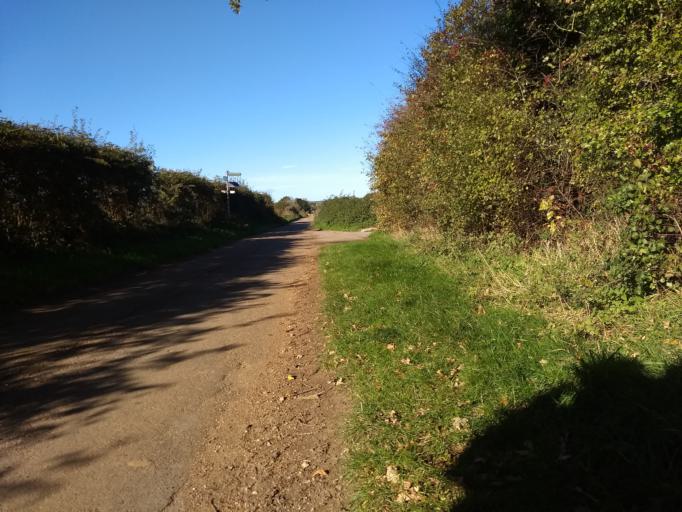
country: GB
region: England
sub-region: Isle of Wight
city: Newport
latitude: 50.6684
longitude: -1.2808
